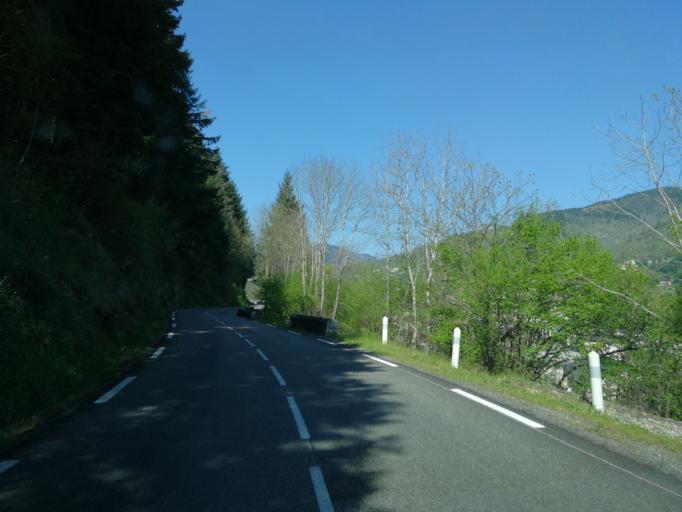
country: FR
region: Rhone-Alpes
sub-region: Departement de l'Ardeche
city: Le Cheylard
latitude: 44.9106
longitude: 4.4473
